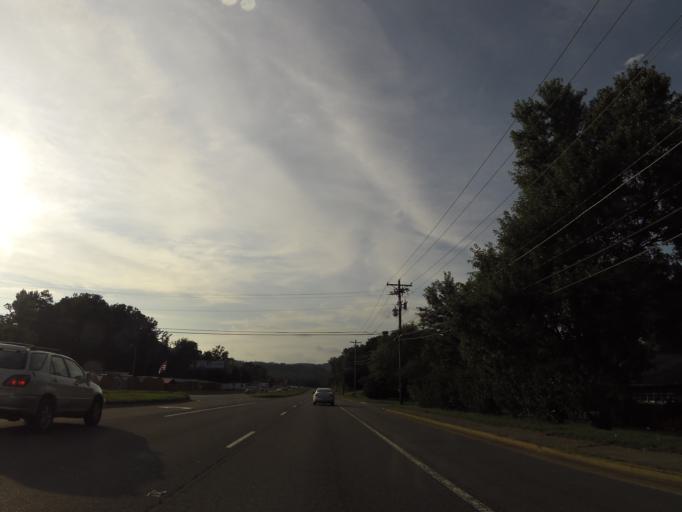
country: US
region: Tennessee
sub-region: Anderson County
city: Oak Ridge
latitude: 35.9847
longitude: -84.1853
